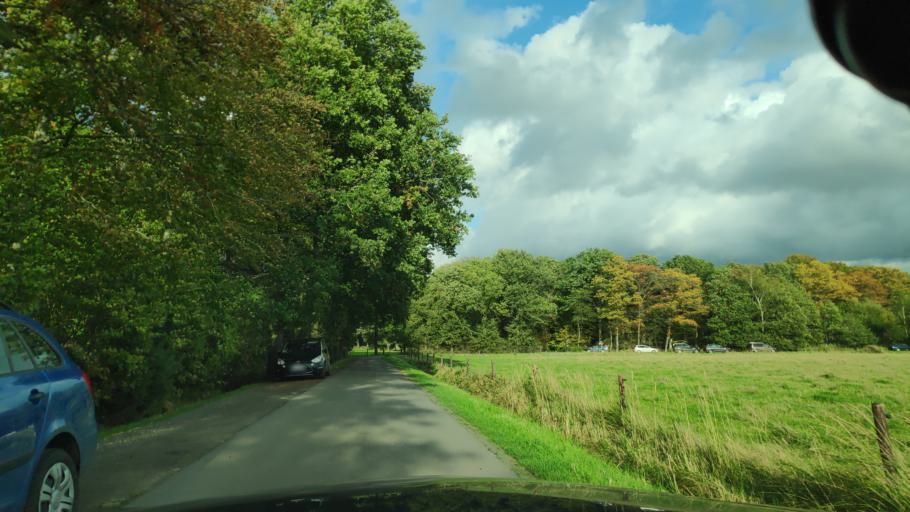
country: BE
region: Flanders
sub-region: Provincie Oost-Vlaanderen
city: Knesselare
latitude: 51.1491
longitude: 3.4477
